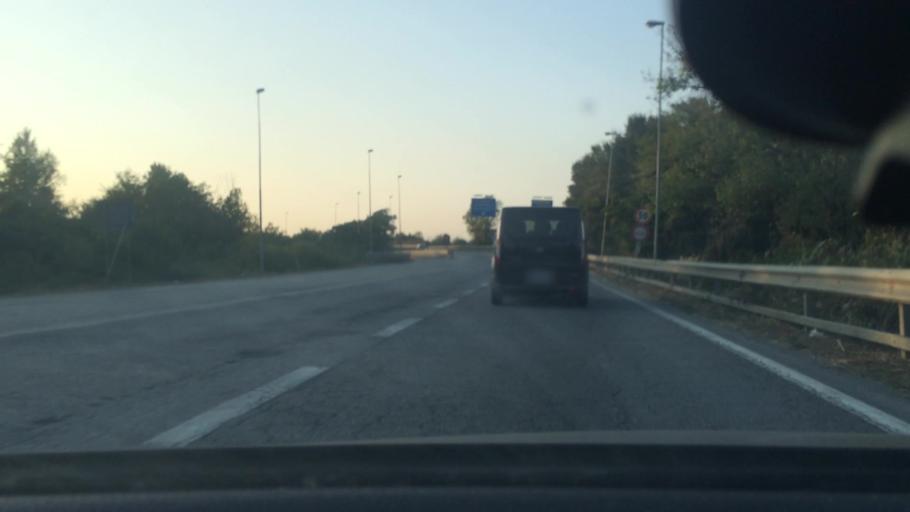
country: IT
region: Lombardy
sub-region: Provincia di Bergamo
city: Grassobbio
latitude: 45.6552
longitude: 9.7373
